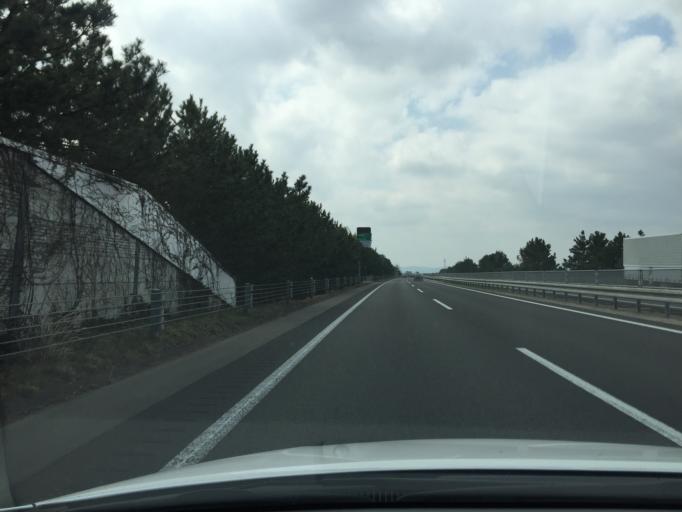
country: JP
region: Miyagi
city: Iwanuma
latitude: 38.1717
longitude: 140.9208
